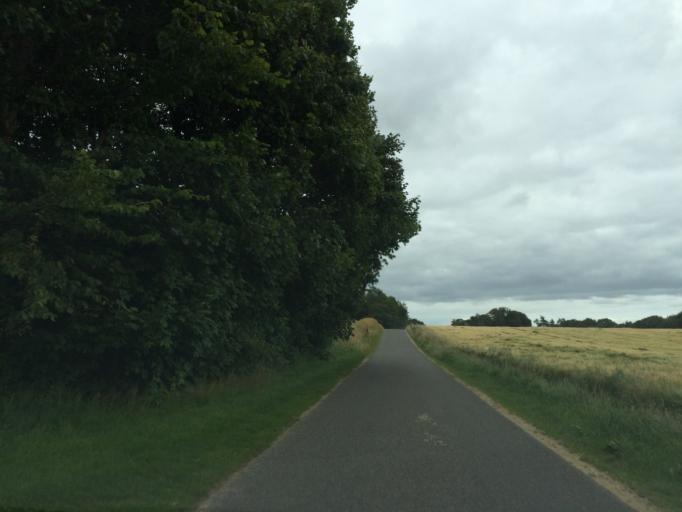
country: DK
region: Central Jutland
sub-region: Silkeborg Kommune
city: Svejbaek
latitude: 56.2062
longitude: 9.6383
